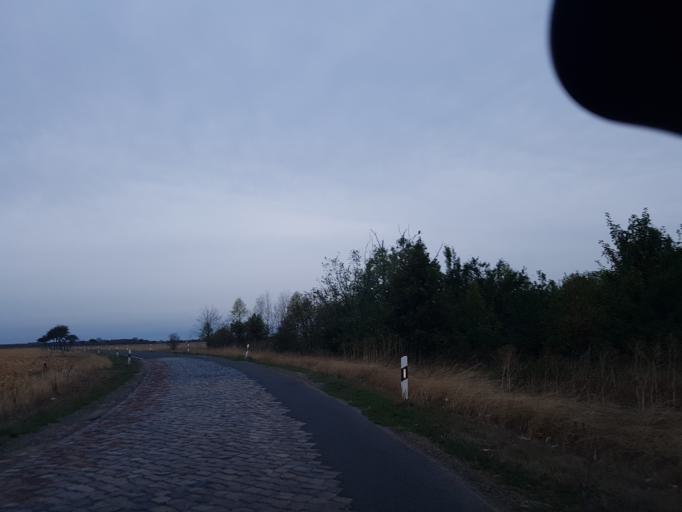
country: DE
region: Saxony
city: Belgern
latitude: 51.4978
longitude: 13.1785
